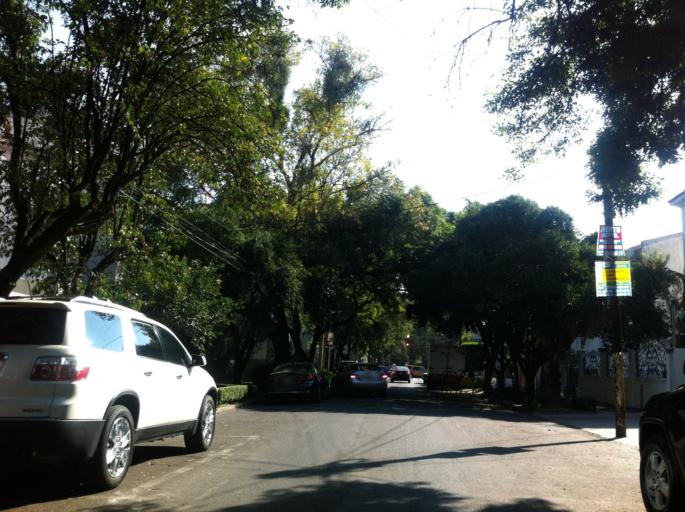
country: MX
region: Mexico City
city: Miguel Hidalgo
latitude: 19.4325
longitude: -99.1926
